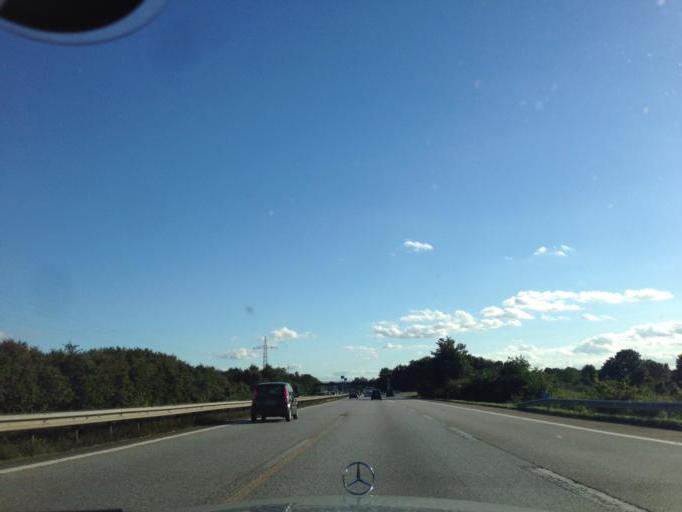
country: DE
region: Schleswig-Holstein
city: Wasbek
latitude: 54.0739
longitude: 9.9234
